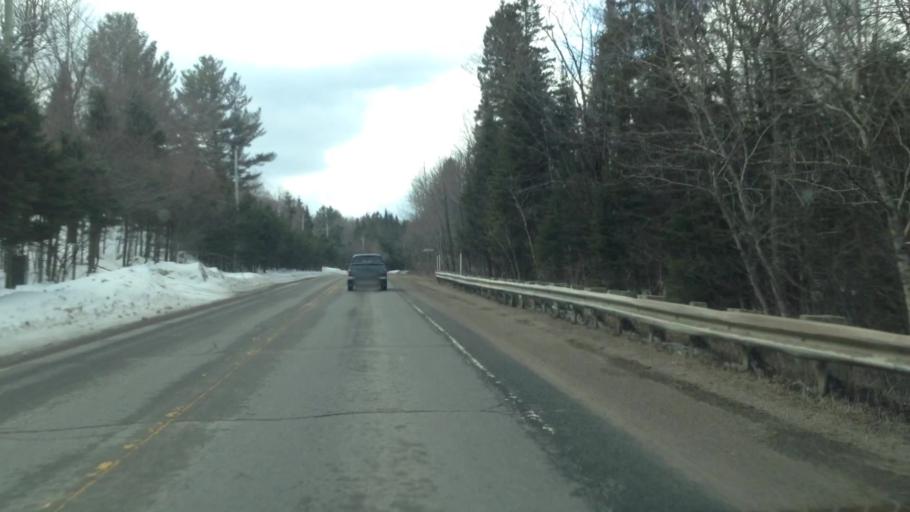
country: CA
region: Quebec
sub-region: Laurentides
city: Brownsburg-Chatham
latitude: 45.7259
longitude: -74.4656
